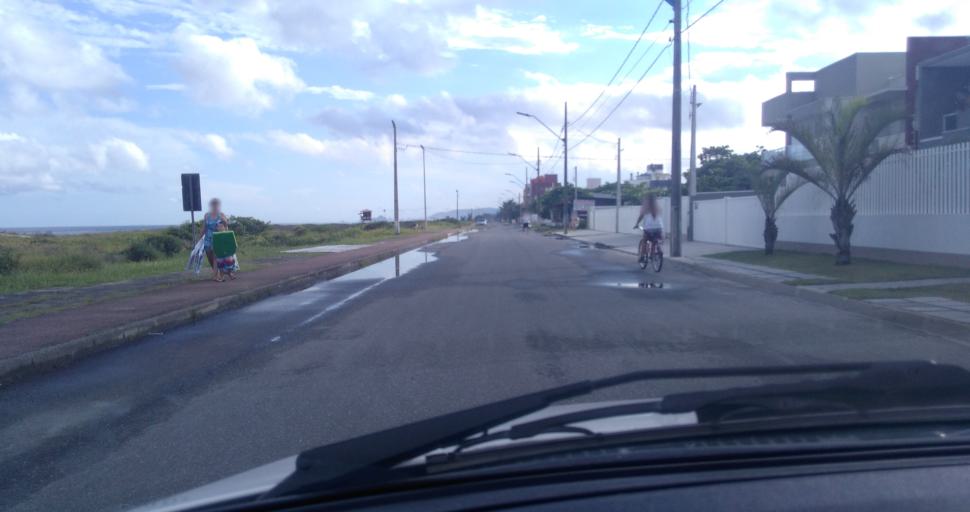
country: BR
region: Parana
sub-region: Pontal Do Parana
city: Pontal do Parana
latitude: -25.7305
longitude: -48.4887
